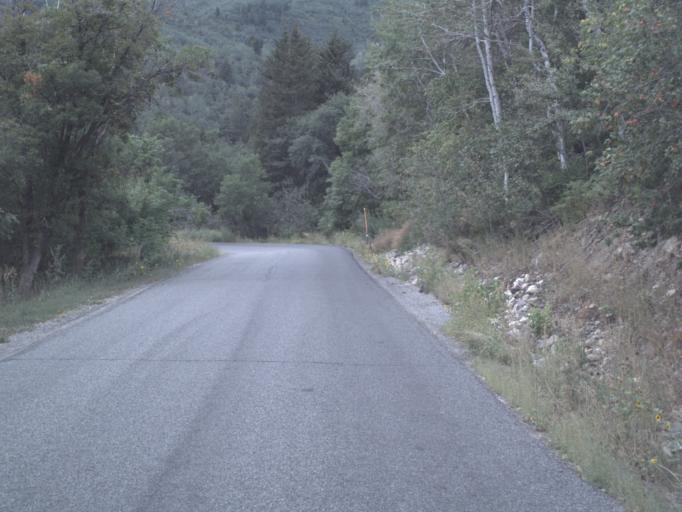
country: US
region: Utah
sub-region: Utah County
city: Lindon
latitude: 40.3974
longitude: -111.5883
